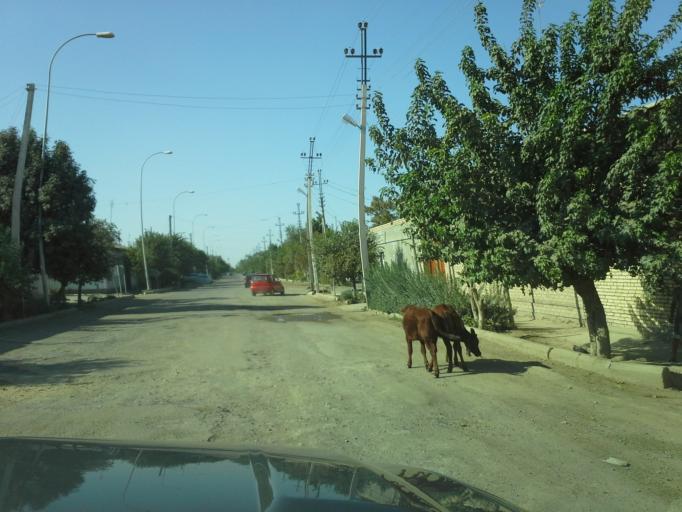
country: TM
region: Dasoguz
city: Dasoguz
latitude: 41.8259
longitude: 59.9800
